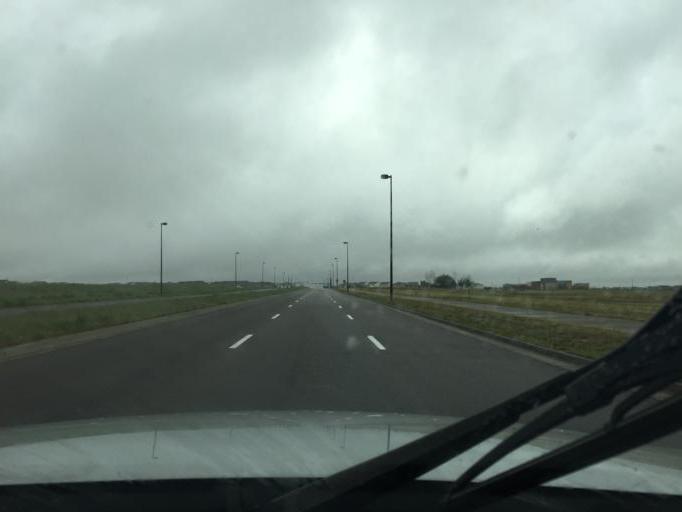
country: US
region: Colorado
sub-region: Adams County
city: Aurora
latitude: 39.7983
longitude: -104.7690
